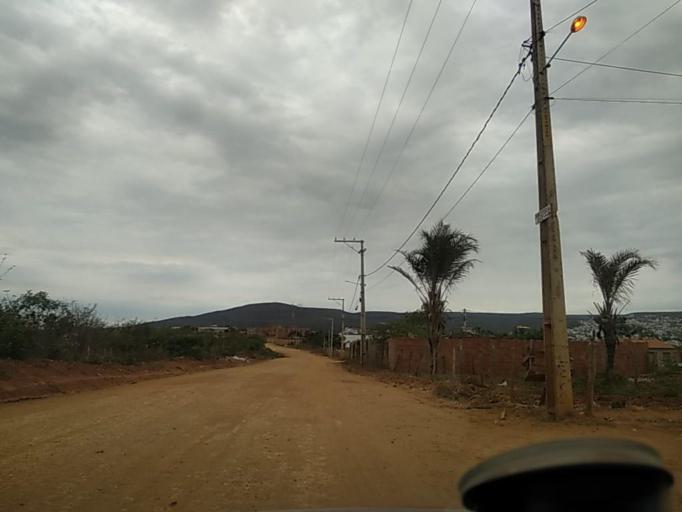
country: BR
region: Bahia
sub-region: Caetite
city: Caetite
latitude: -14.0489
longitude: -42.4735
